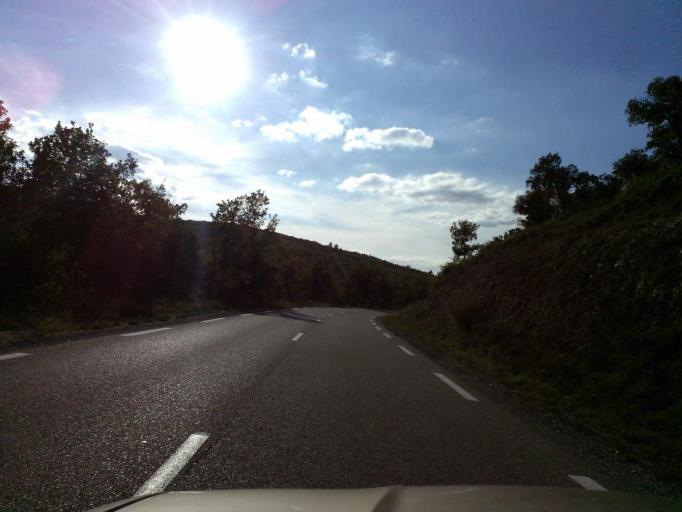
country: FR
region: Provence-Alpes-Cote d'Azur
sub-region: Departement des Alpes-de-Haute-Provence
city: Greoux-les-Bains
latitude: 43.8056
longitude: 5.8890
